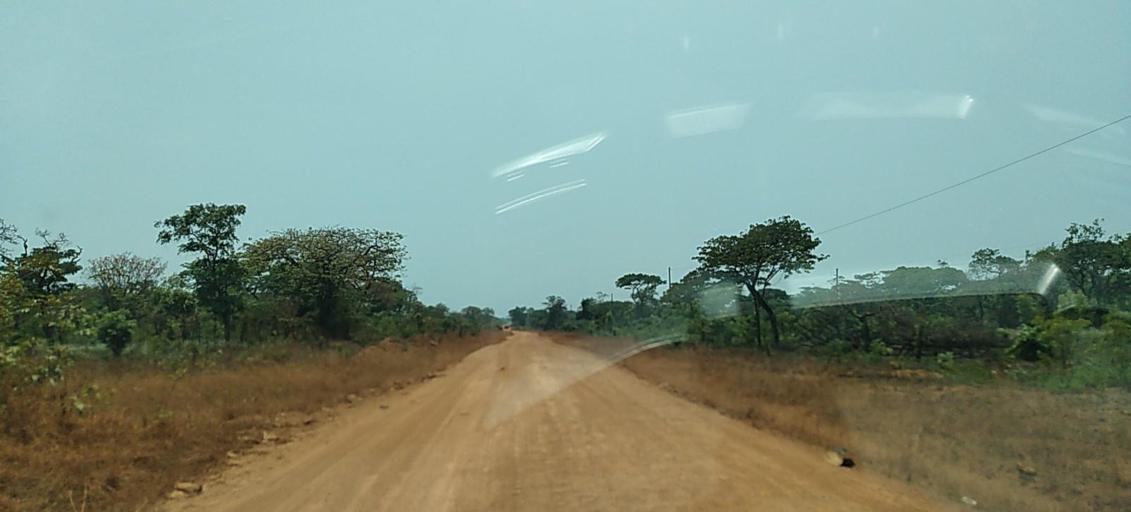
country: CD
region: Katanga
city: Kipushi
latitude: -11.9278
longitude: 26.9944
